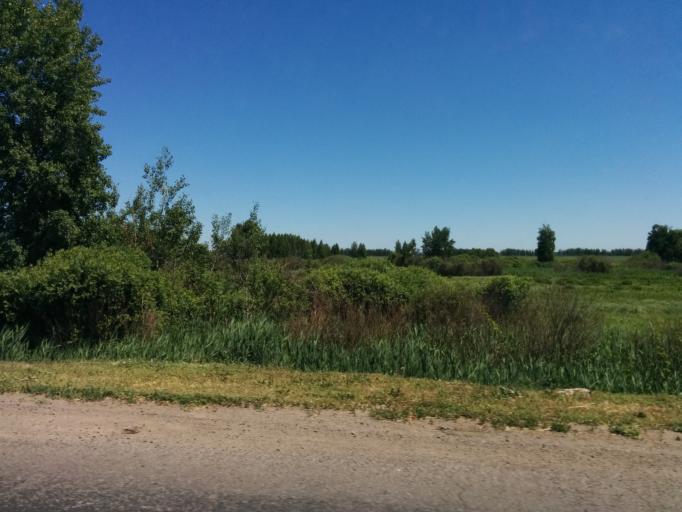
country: RU
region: Tambov
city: Goreloye
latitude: 52.8882
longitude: 41.4700
